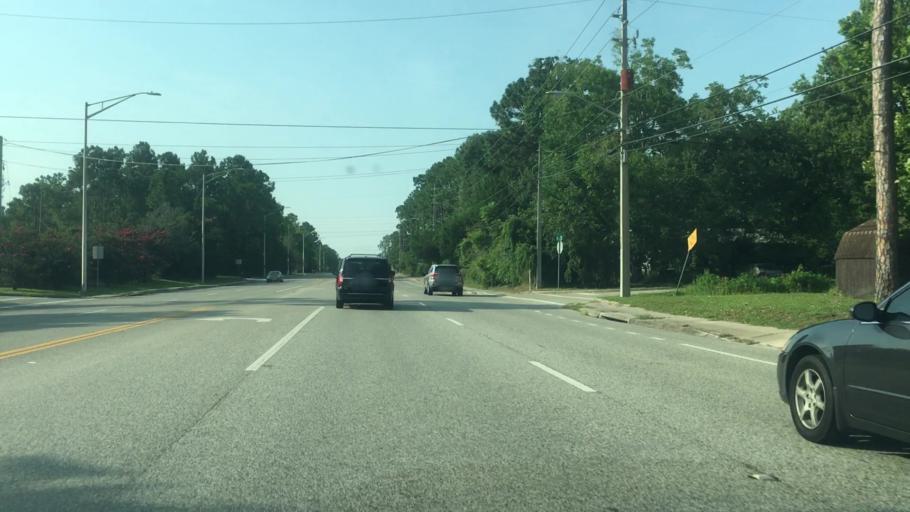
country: US
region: Florida
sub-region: Duval County
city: Neptune Beach
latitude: 30.2922
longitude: -81.4589
